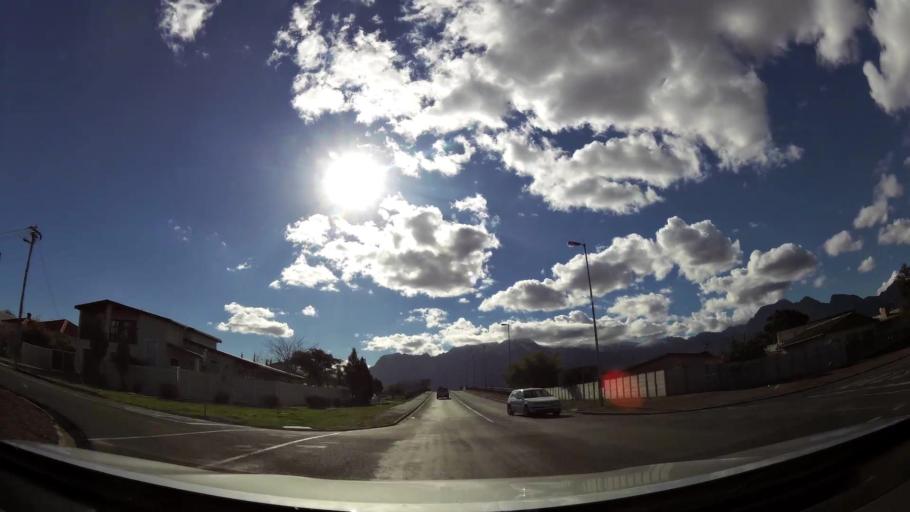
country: ZA
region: Western Cape
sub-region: Cape Winelands District Municipality
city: Worcester
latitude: -33.6414
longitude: 19.4324
